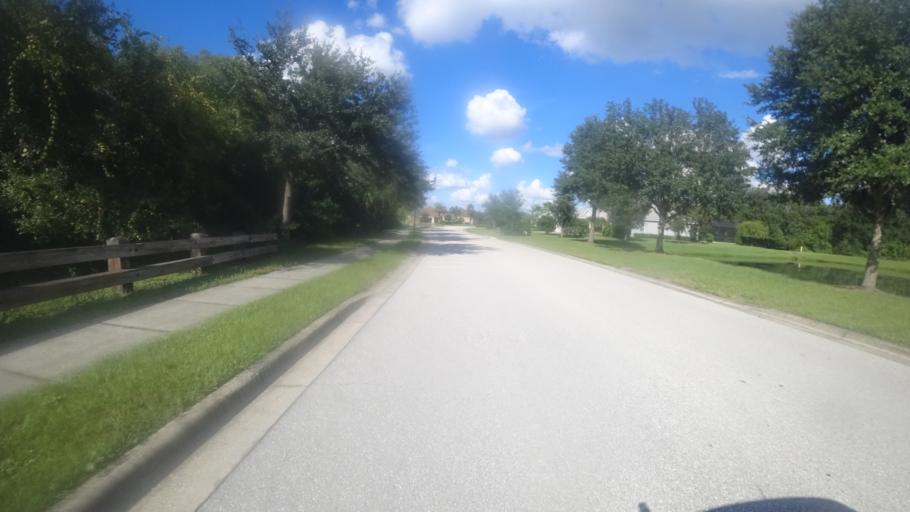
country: US
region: Florida
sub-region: Manatee County
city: Ellenton
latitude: 27.5407
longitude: -82.3799
